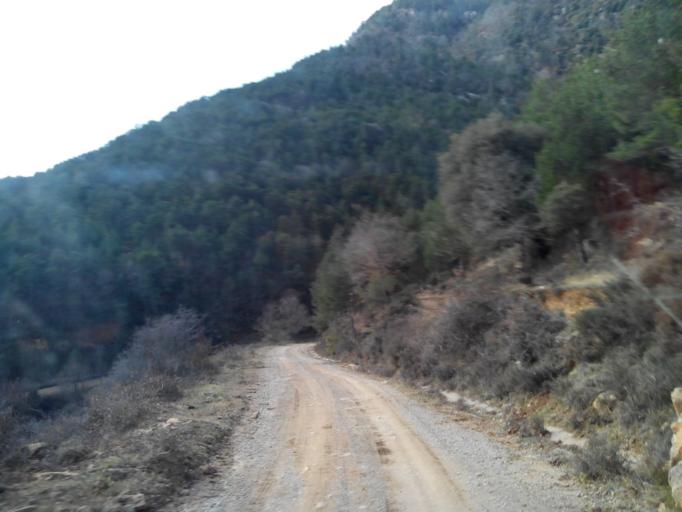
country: ES
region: Catalonia
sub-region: Provincia de Barcelona
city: Vilada
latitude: 42.1608
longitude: 1.9277
